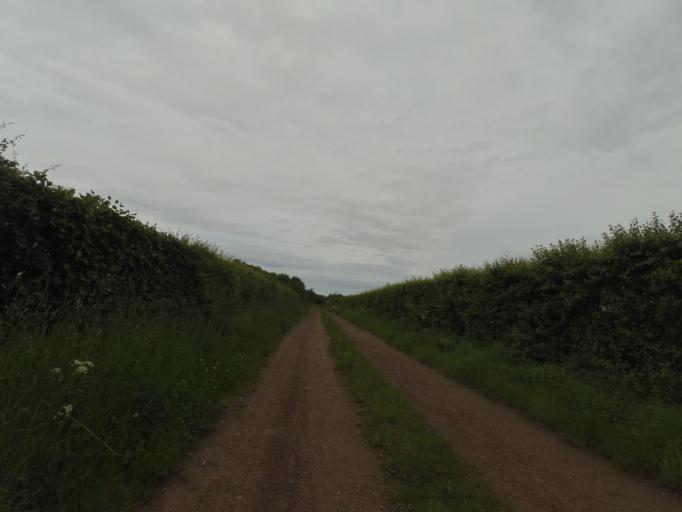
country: GB
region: Scotland
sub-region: East Lothian
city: Macmerry
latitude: 55.9472
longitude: -2.9248
